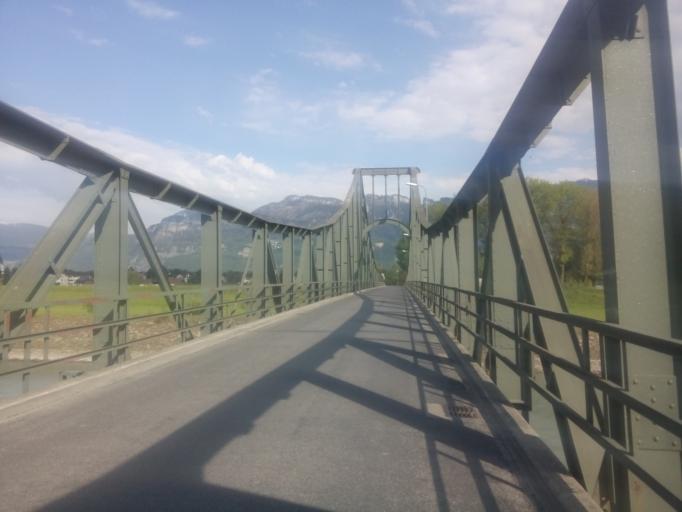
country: CH
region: Saint Gallen
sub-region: Wahlkreis Rheintal
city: Diepoldsau
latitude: 47.3832
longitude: 9.6415
